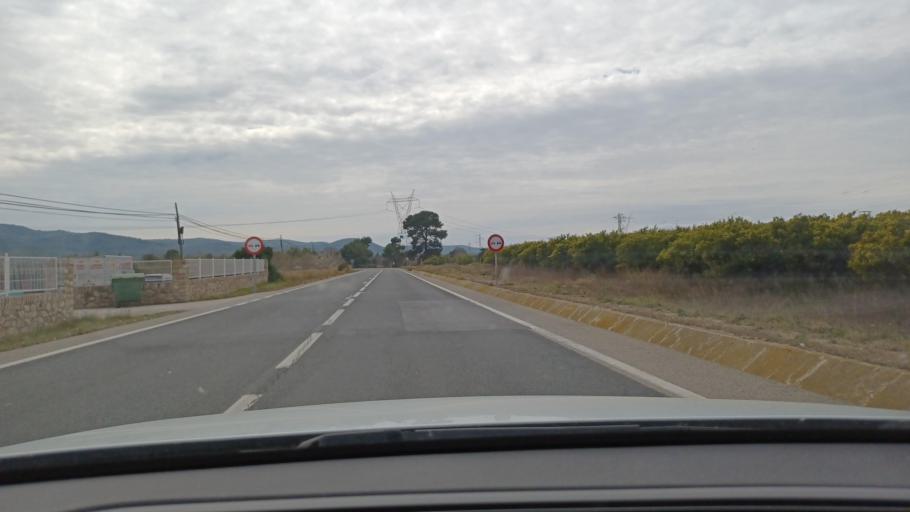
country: ES
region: Catalonia
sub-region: Provincia de Tarragona
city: Santa Barbara
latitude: 40.6953
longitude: 0.4757
